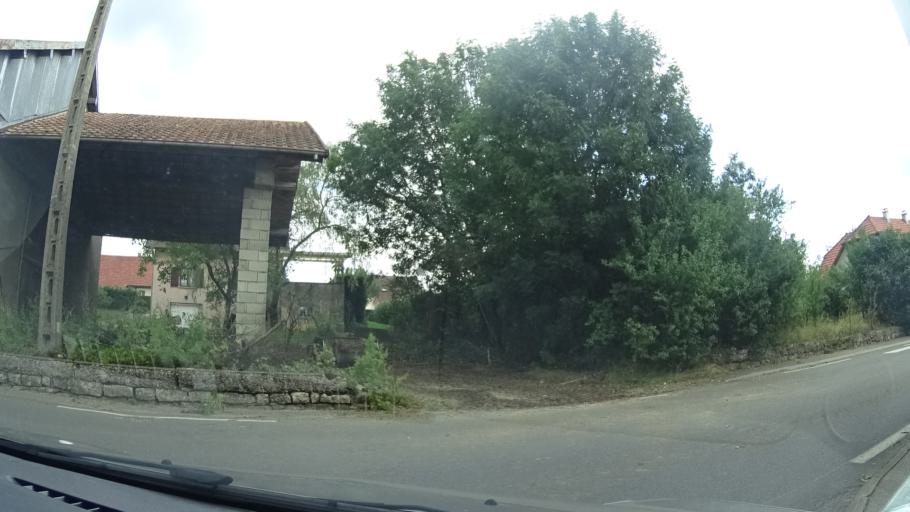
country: FR
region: Franche-Comte
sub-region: Departement du Doubs
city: Saone
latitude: 47.2202
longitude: 6.1128
